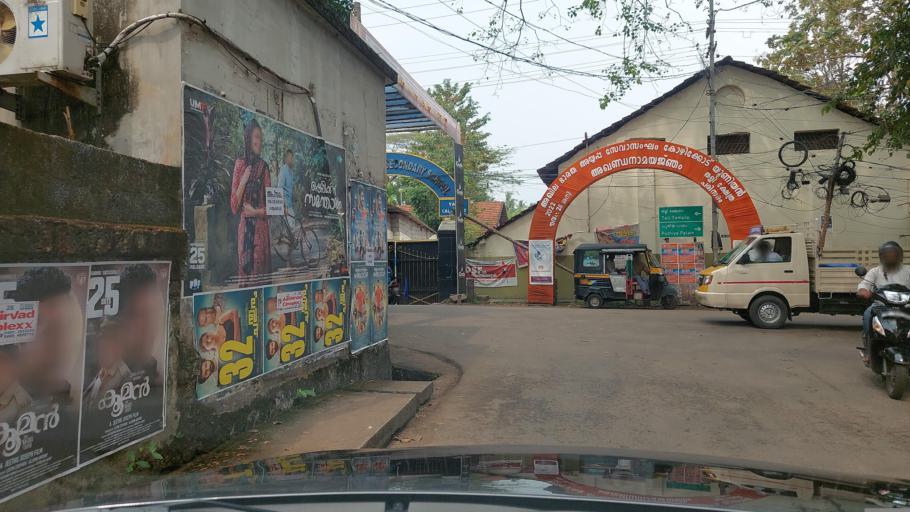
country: IN
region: Kerala
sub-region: Kozhikode
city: Kozhikode
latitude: 11.2475
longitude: 75.7883
